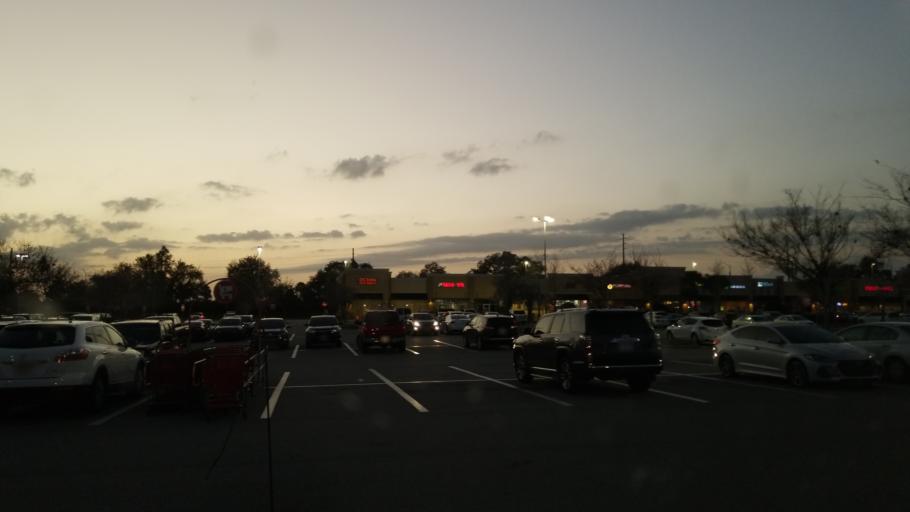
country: US
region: Florida
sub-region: Polk County
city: Citrus Ridge
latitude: 28.3447
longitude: -81.6135
